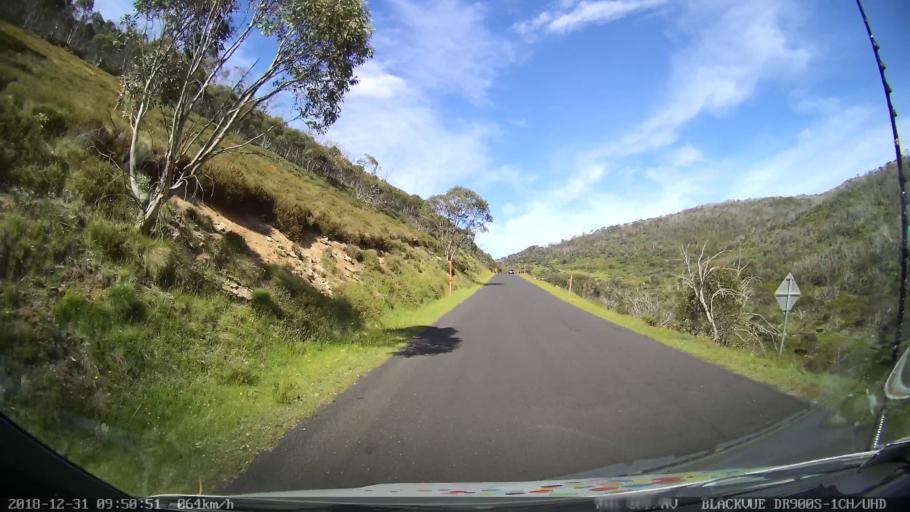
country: AU
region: New South Wales
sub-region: Snowy River
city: Jindabyne
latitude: -36.5222
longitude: 148.2683
